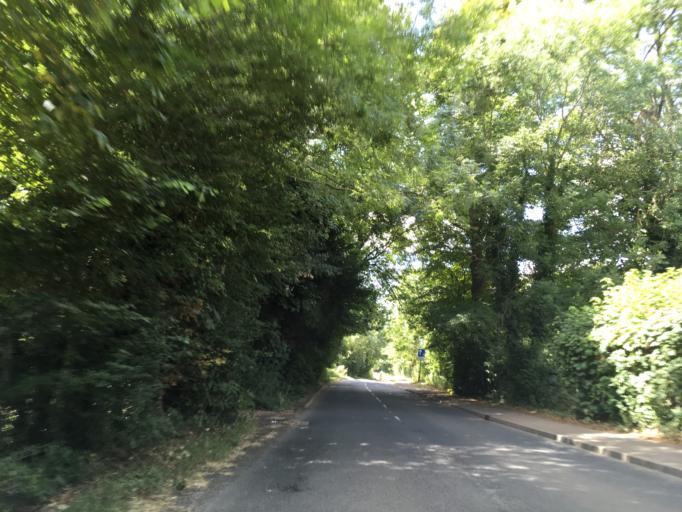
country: GB
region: England
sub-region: Gloucestershire
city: Barnwood
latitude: 51.8313
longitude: -2.2033
